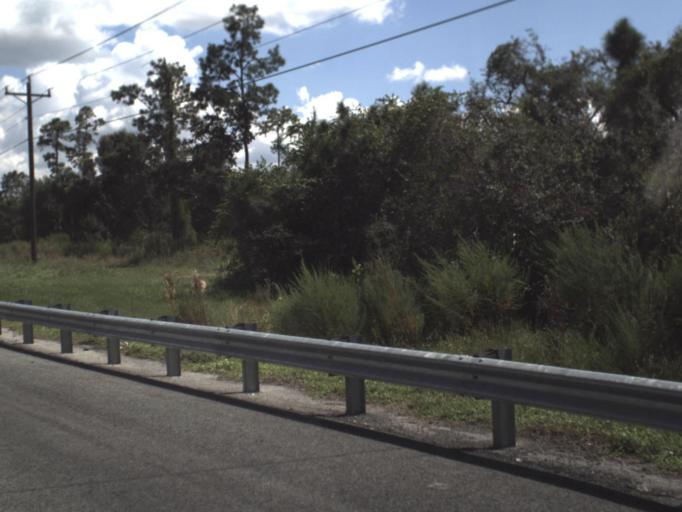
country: US
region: Florida
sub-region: Lee County
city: Palmona Park
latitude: 26.6822
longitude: -81.9087
